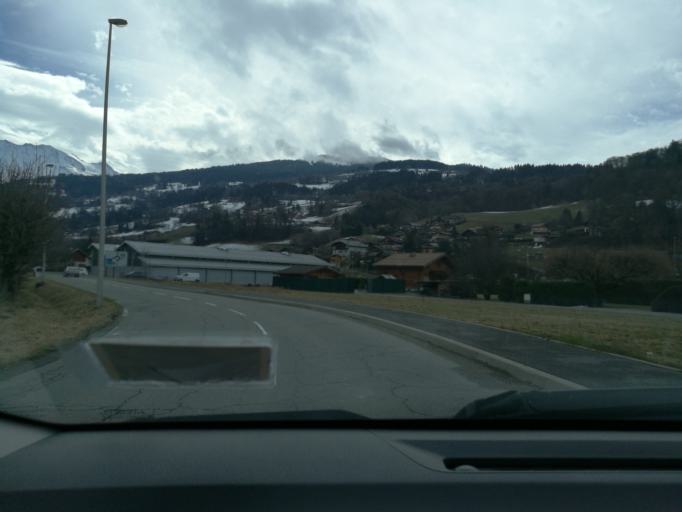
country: FR
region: Rhone-Alpes
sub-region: Departement de la Haute-Savoie
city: Domancy
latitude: 45.9122
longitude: 6.6573
